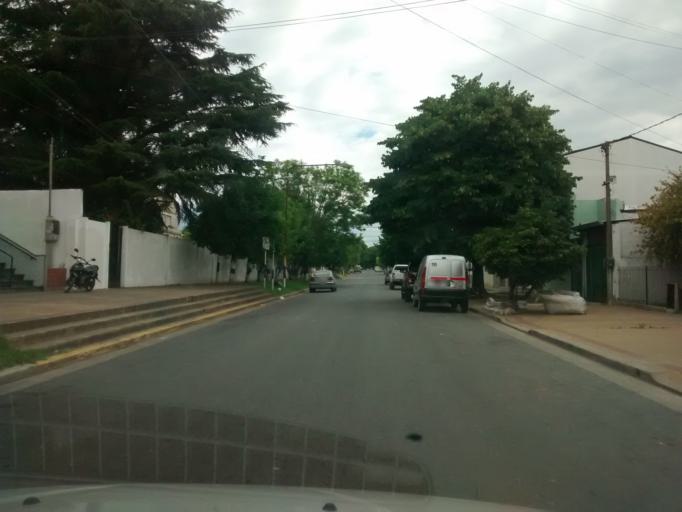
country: AR
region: Buenos Aires
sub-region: Partido de La Plata
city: La Plata
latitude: -34.9284
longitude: -57.9209
